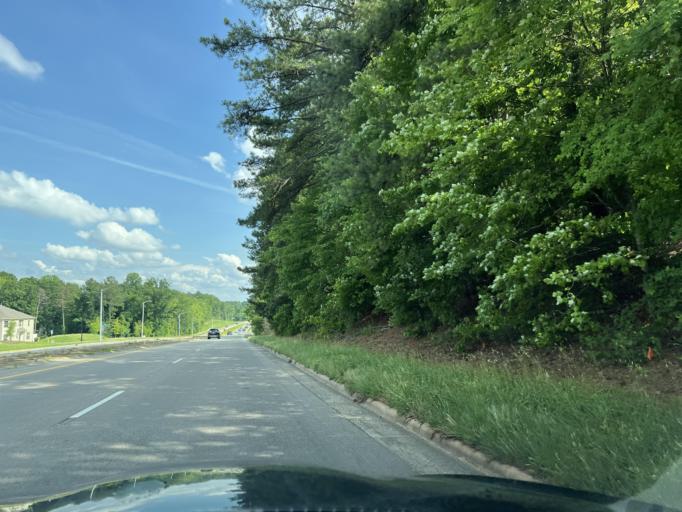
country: US
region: North Carolina
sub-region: Durham County
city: Durham
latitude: 35.9518
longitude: -78.8900
